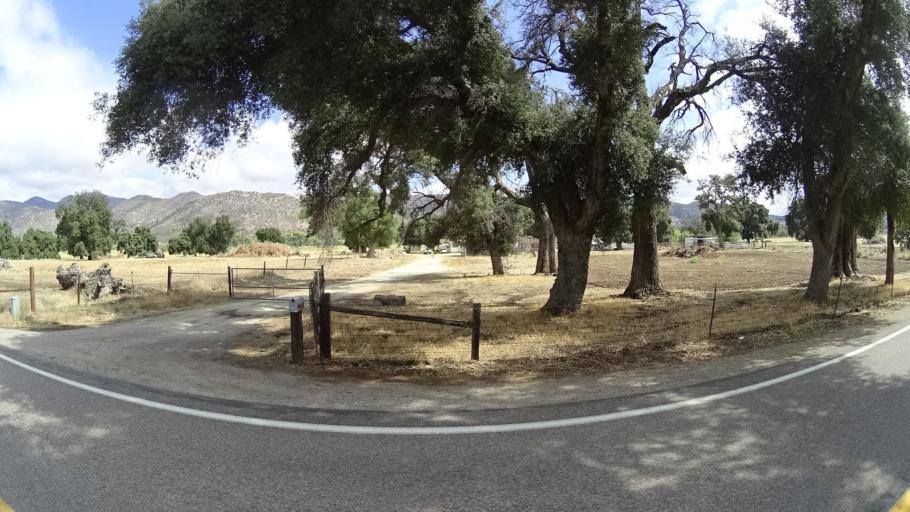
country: US
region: California
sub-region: San Diego County
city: Pine Valley
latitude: 32.7430
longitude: -116.4943
